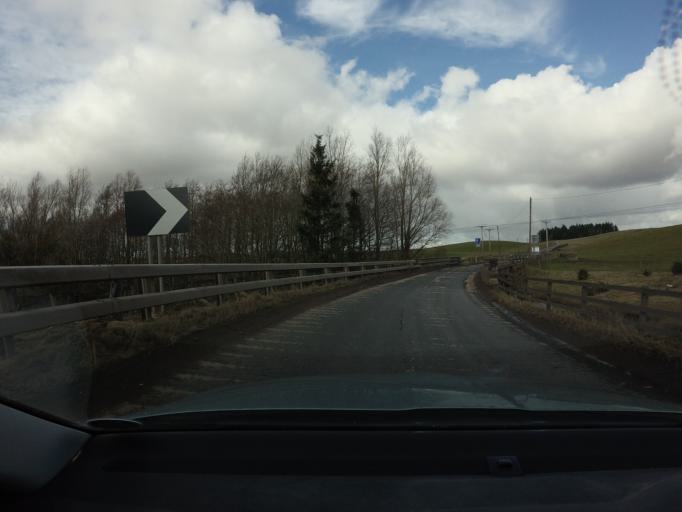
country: GB
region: Scotland
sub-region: South Lanarkshire
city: Lanark
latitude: 55.6406
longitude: -3.7421
